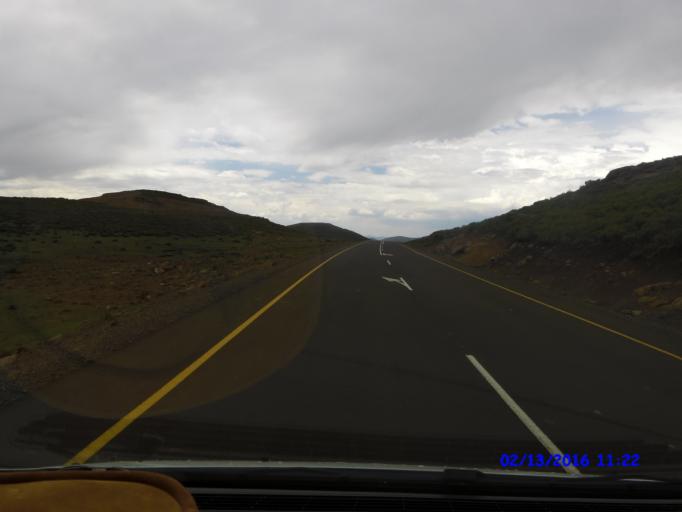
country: LS
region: Maseru
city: Nako
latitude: -29.7592
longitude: 27.9811
